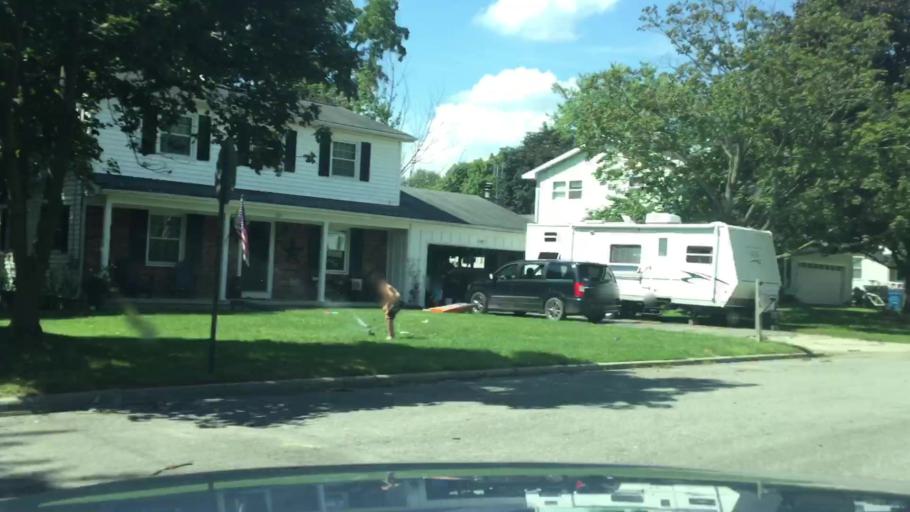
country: US
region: Michigan
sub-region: Lenawee County
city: Clinton
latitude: 42.0741
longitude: -83.9691
